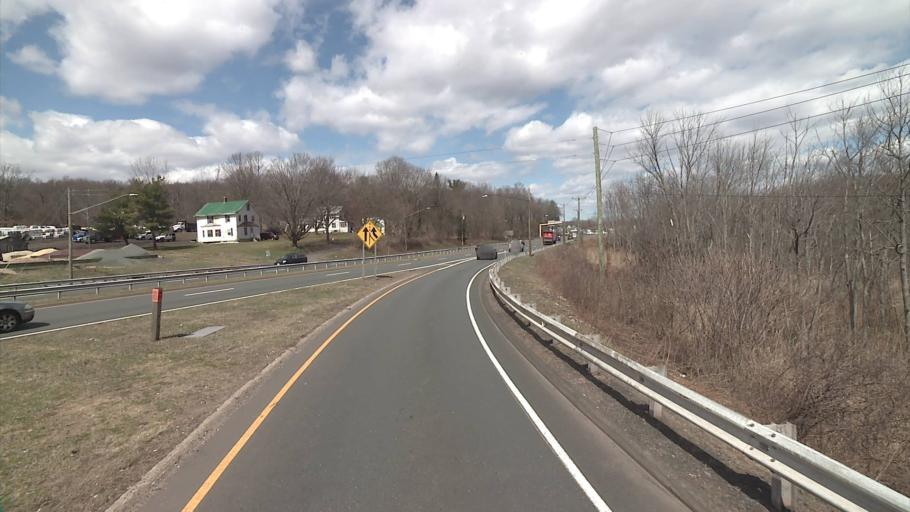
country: US
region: Connecticut
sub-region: Hartford County
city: Newington
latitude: 41.6997
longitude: -72.7038
